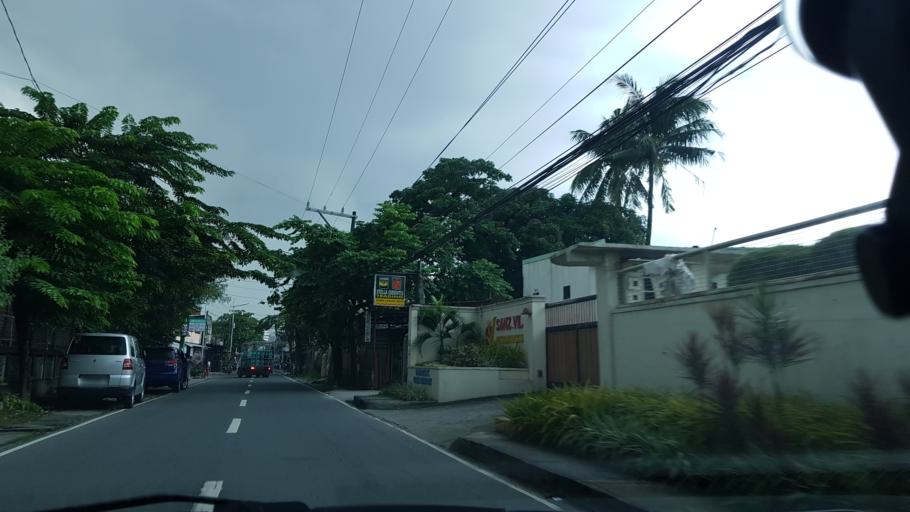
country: PH
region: Calabarzon
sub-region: Province of Rizal
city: Pateros
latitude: 14.5370
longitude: 121.0691
